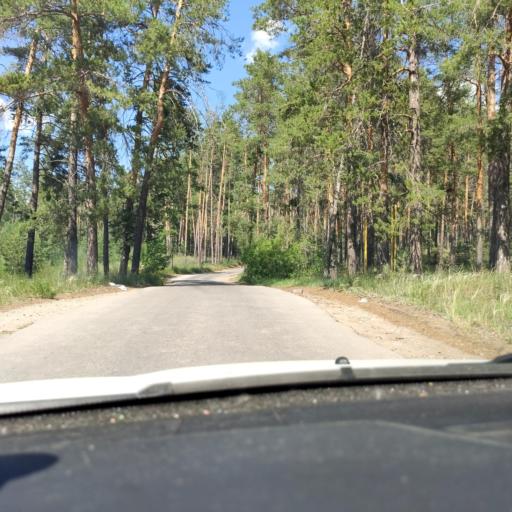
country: RU
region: Samara
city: Pribrezhnyy
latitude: 53.4800
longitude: 49.8251
